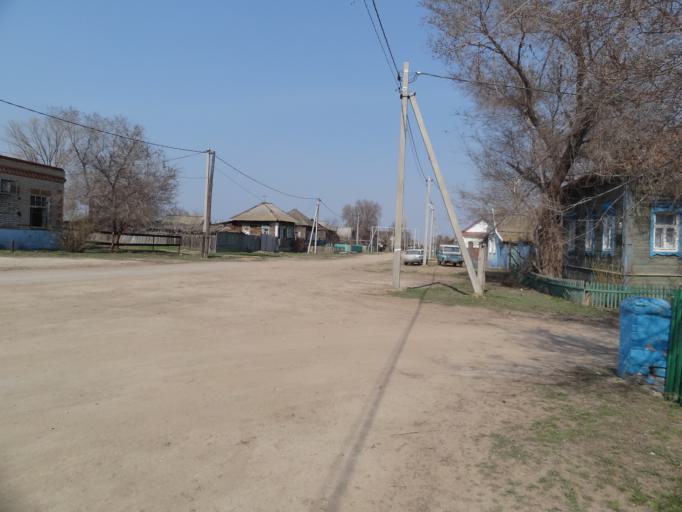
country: RU
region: Saratov
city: Privolzhskiy
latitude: 51.3050
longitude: 45.9603
